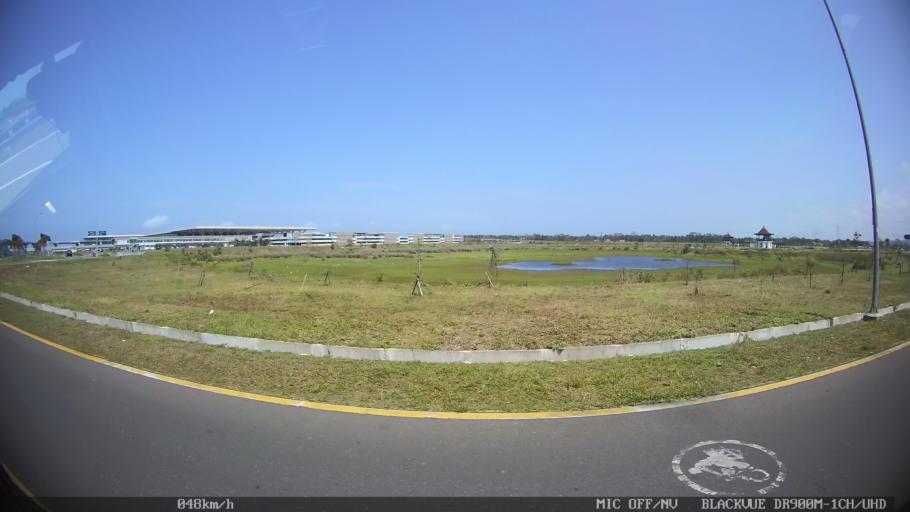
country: ID
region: Daerah Istimewa Yogyakarta
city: Srandakan
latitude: -7.8946
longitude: 110.0641
